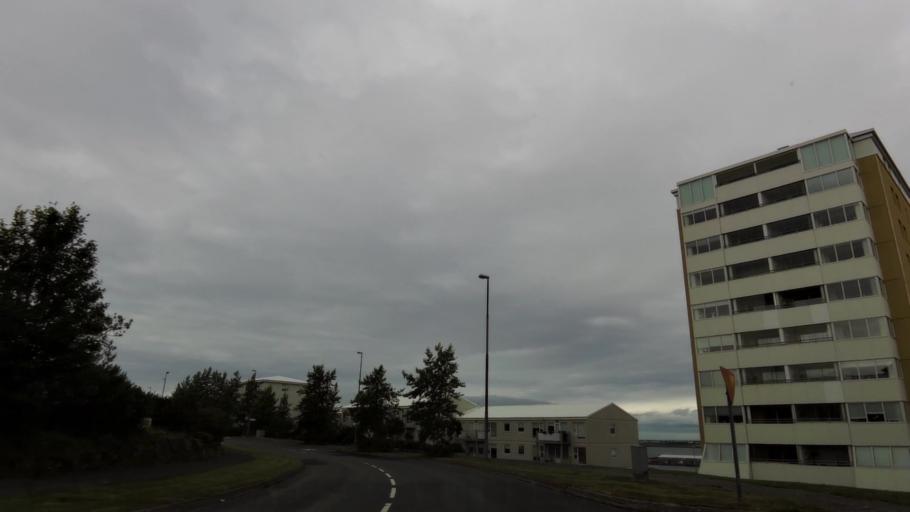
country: IS
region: Capital Region
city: Hafnarfjoerdur
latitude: 64.0573
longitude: -21.9832
